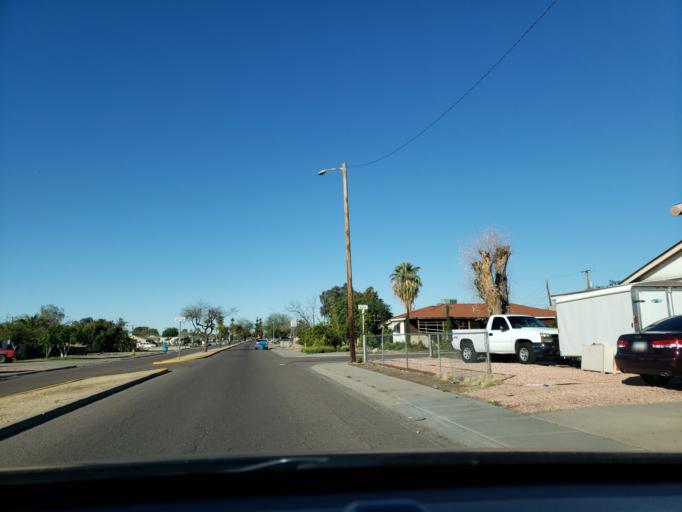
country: US
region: Arizona
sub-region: Maricopa County
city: Glendale
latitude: 33.5604
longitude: -112.1175
